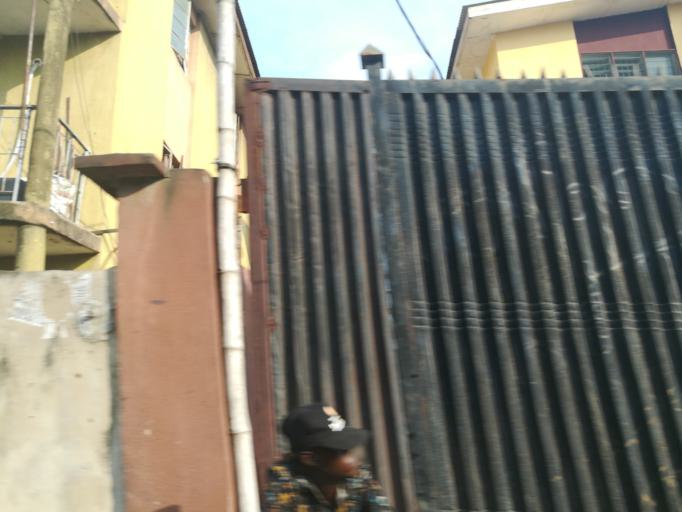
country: NG
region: Lagos
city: Ojota
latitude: 6.5926
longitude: 3.3967
